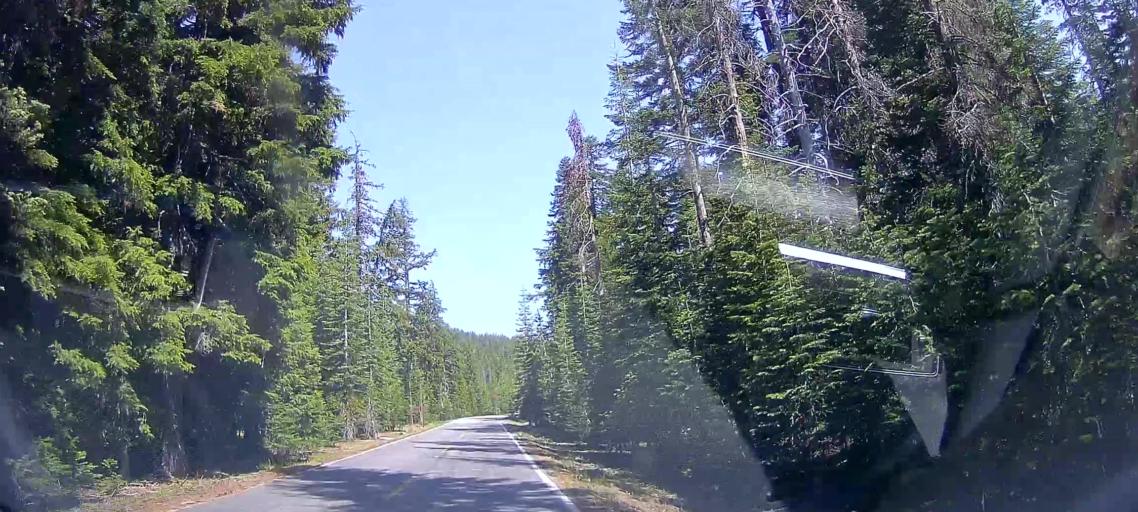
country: US
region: Oregon
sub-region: Jackson County
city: Shady Cove
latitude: 42.8929
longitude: -122.1337
